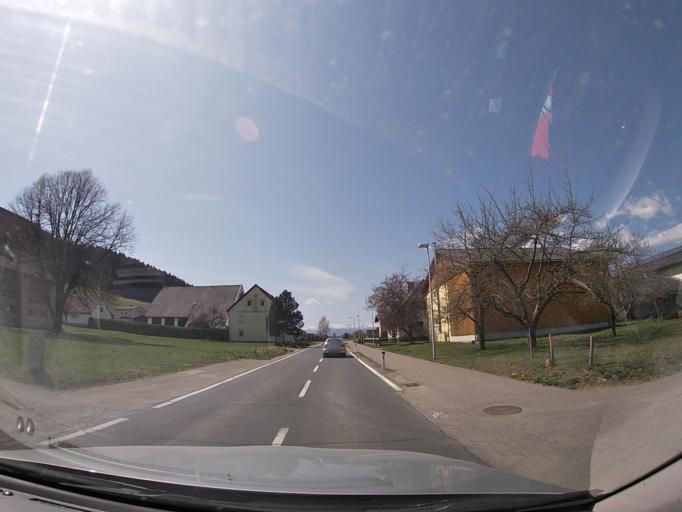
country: AT
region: Styria
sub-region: Politischer Bezirk Murtal
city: Sankt Margarethen bei Knittelfeld
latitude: 47.2330
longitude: 14.8671
